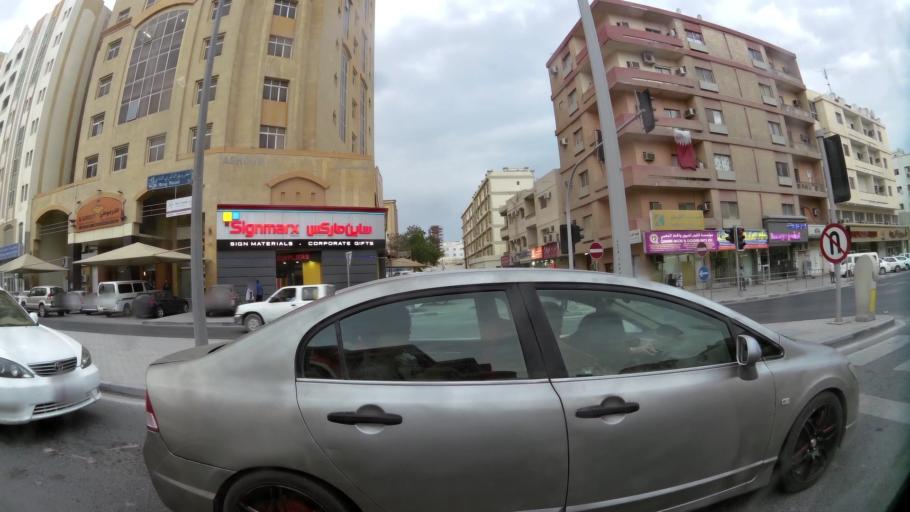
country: QA
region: Baladiyat ad Dawhah
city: Doha
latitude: 25.2747
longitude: 51.5234
